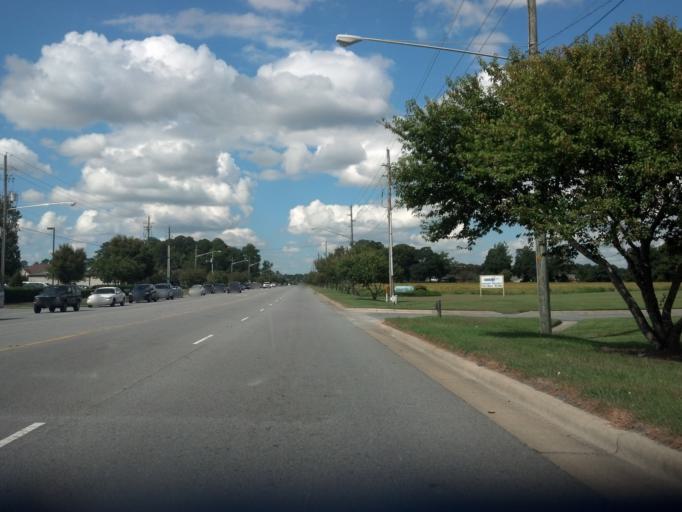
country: US
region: North Carolina
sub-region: Pitt County
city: Windsor
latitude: 35.5683
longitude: -77.3512
